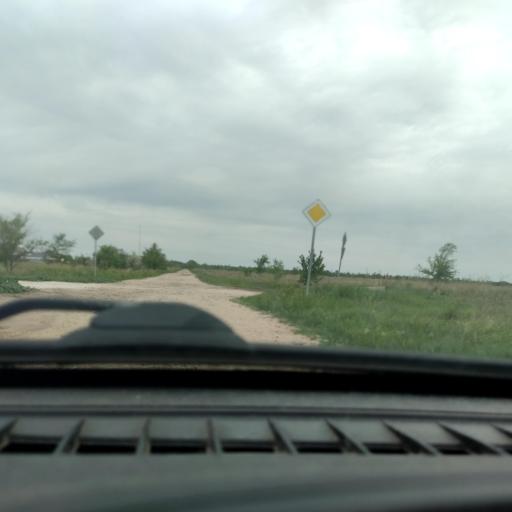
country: RU
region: Samara
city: Podstepki
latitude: 53.5282
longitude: 49.1694
